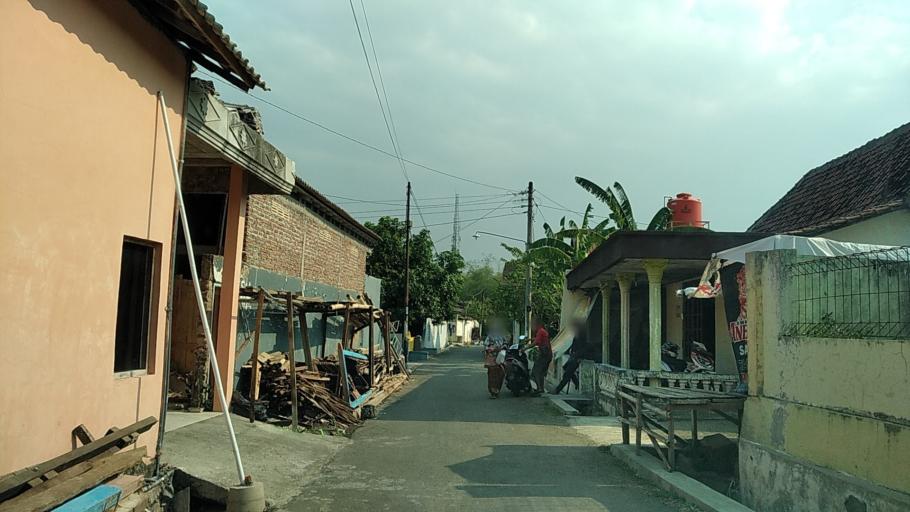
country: ID
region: Central Java
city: Semarang
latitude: -7.0259
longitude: 110.4578
